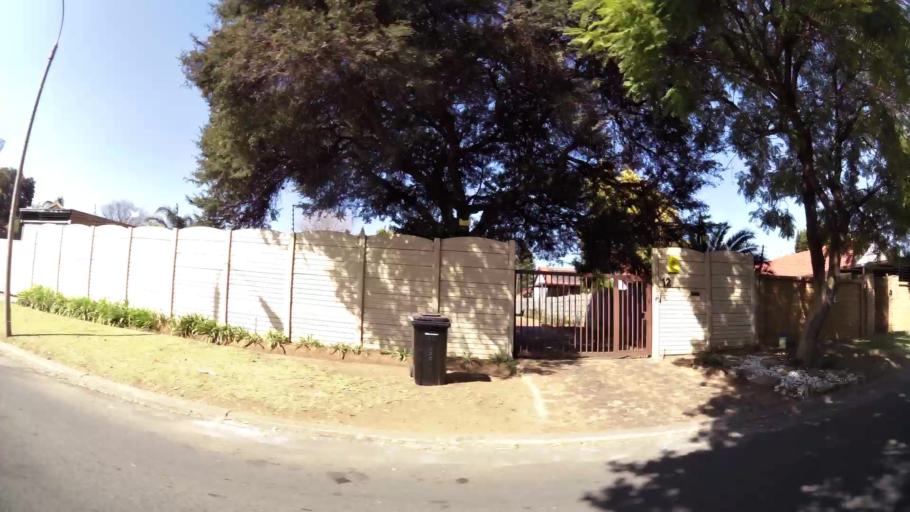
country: ZA
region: Gauteng
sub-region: Ekurhuleni Metropolitan Municipality
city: Tembisa
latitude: -26.0487
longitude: 28.2315
